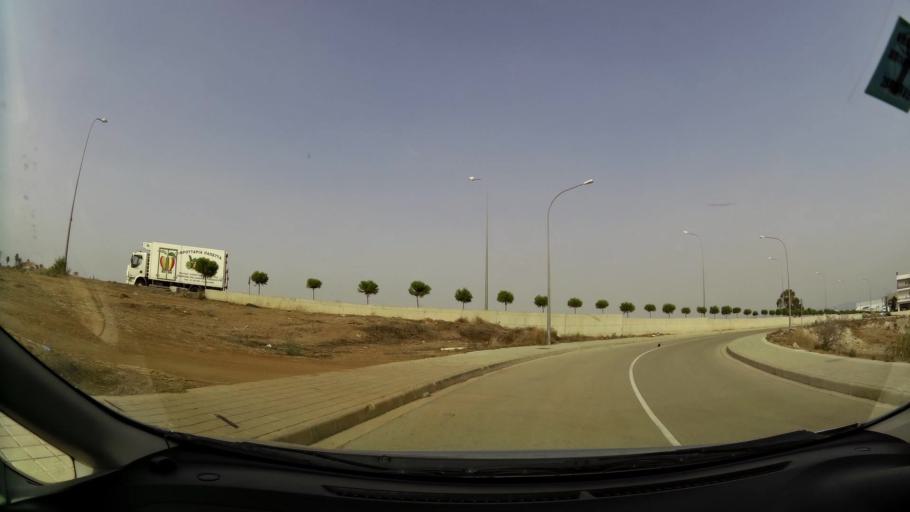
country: CY
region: Lefkosia
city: Geri
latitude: 35.0698
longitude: 33.3821
